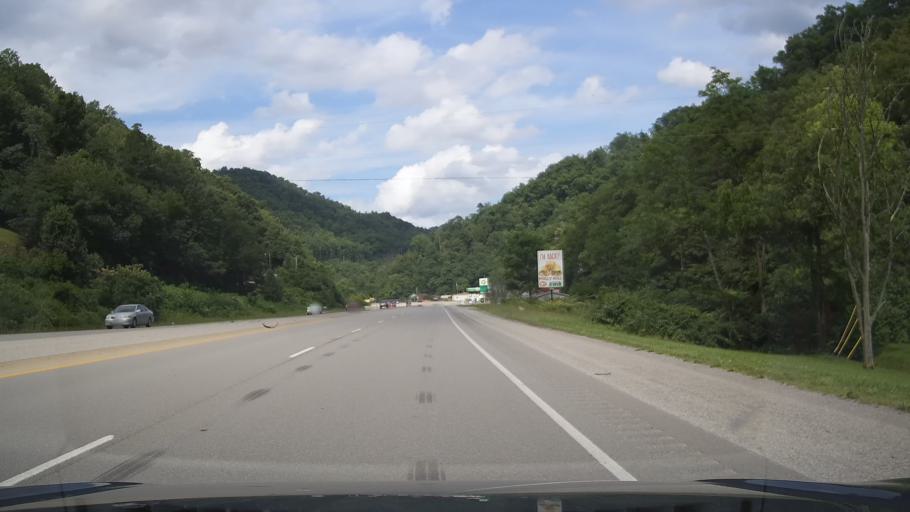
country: US
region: Kentucky
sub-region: Pike County
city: Pikeville
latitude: 37.3408
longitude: -82.5541
